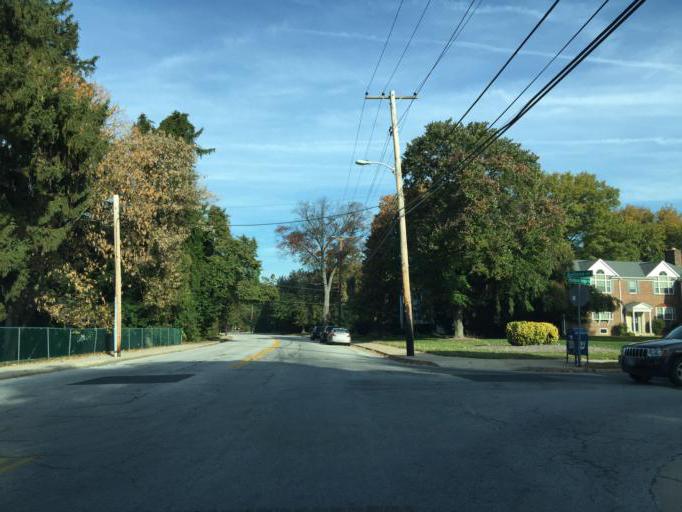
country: US
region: Maryland
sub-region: Baltimore County
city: Towson
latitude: 39.3776
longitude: -76.6211
